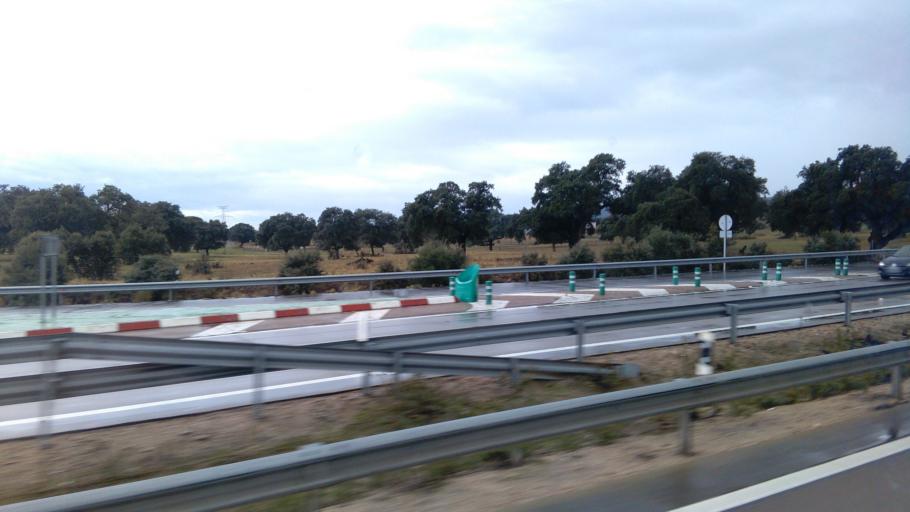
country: ES
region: Castille-La Mancha
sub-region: Province of Toledo
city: Cervera de los Montes
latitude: 40.0131
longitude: -4.7805
